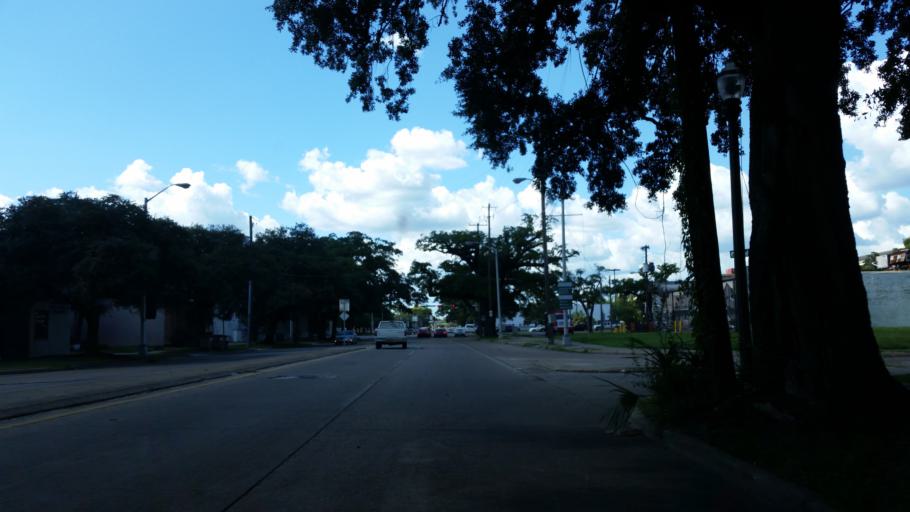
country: US
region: Alabama
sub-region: Mobile County
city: Mobile
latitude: 30.6850
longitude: -88.0530
